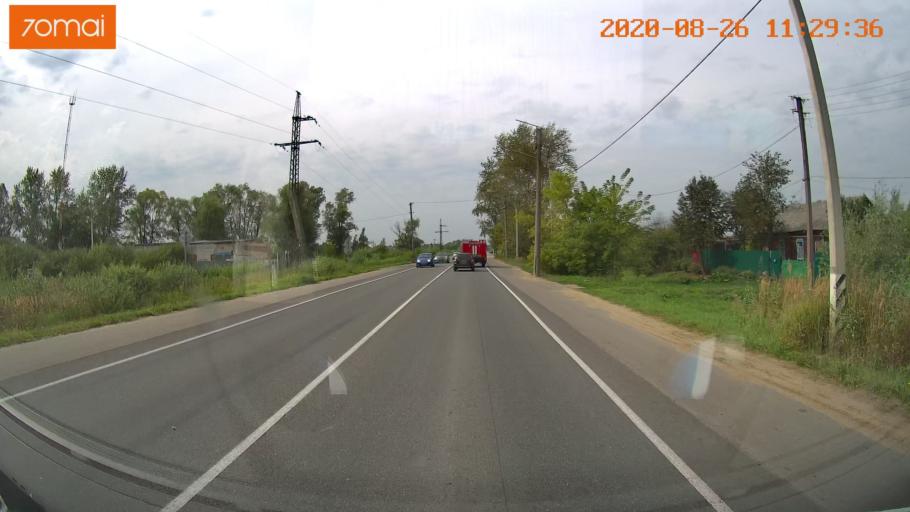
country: RU
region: Rjazan
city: Shilovo
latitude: 54.3189
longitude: 40.8967
